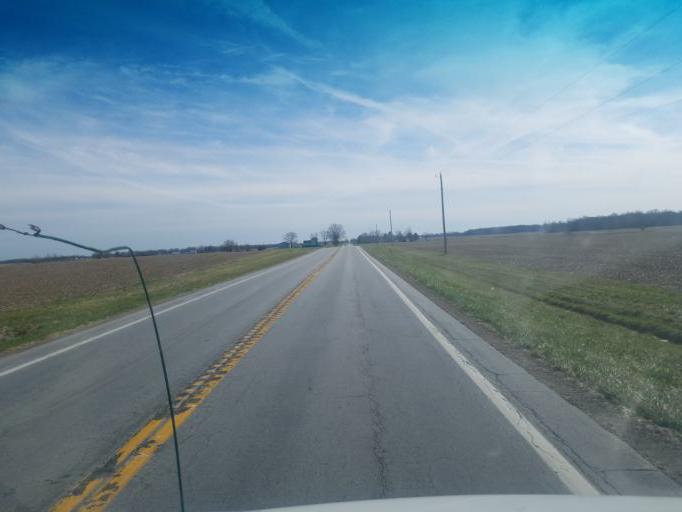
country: US
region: Ohio
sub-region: Union County
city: Richwood
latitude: 40.3758
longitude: -83.2842
